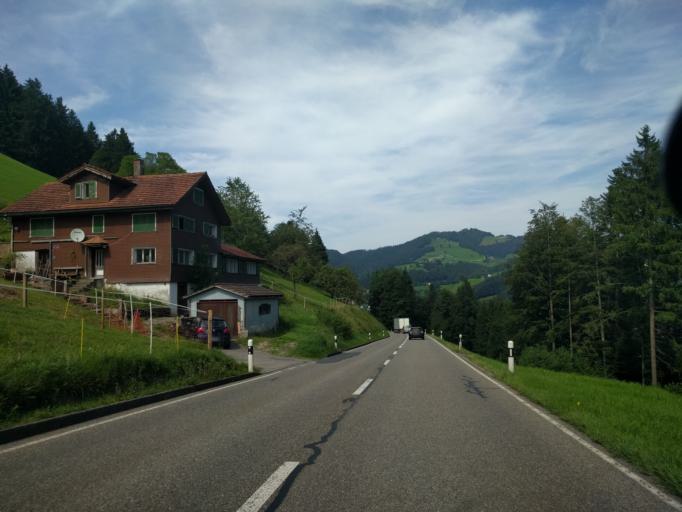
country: CH
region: Saint Gallen
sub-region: Wahlkreis Toggenburg
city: Wattwil
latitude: 47.2879
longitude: 9.0837
